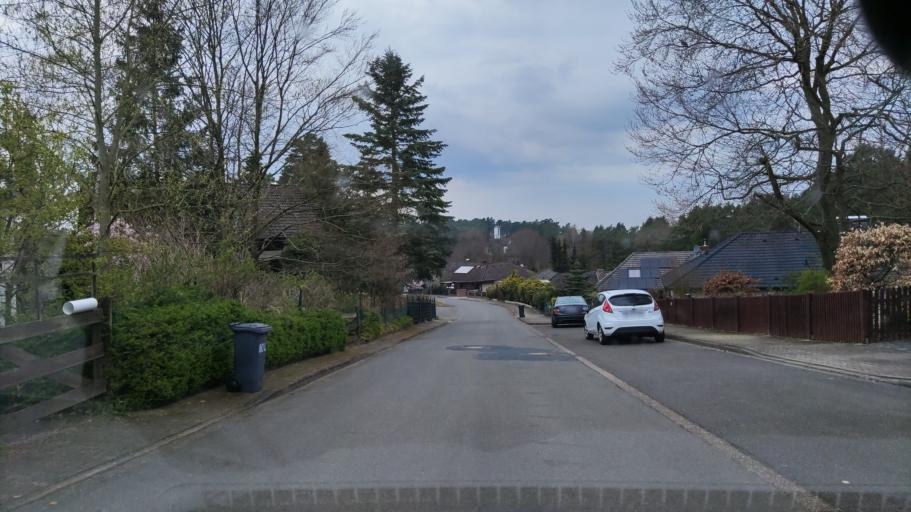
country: DE
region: Lower Saxony
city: Tosterglope
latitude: 53.2632
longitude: 10.7958
